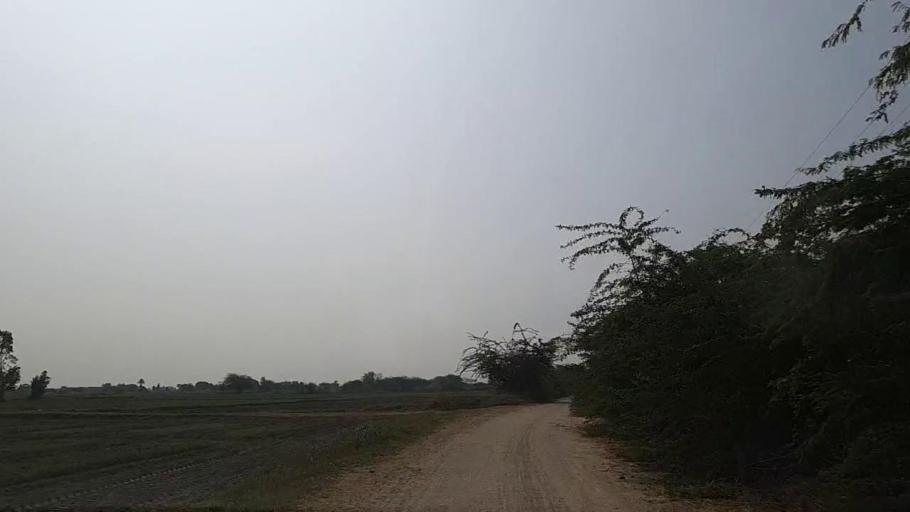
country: PK
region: Sindh
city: Mirpur Sakro
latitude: 24.6103
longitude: 67.7282
